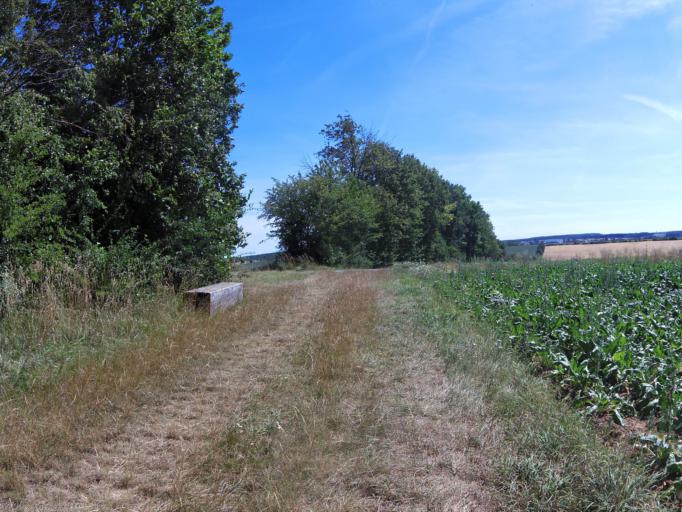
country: DE
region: Bavaria
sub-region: Regierungsbezirk Unterfranken
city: Waldbuttelbrunn
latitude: 49.8073
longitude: 9.8381
